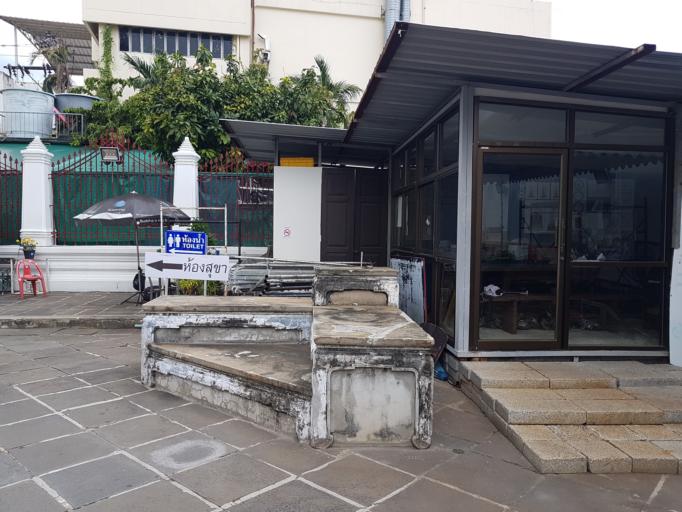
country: TH
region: Bangkok
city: Bangkok
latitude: 13.7436
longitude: 100.4887
